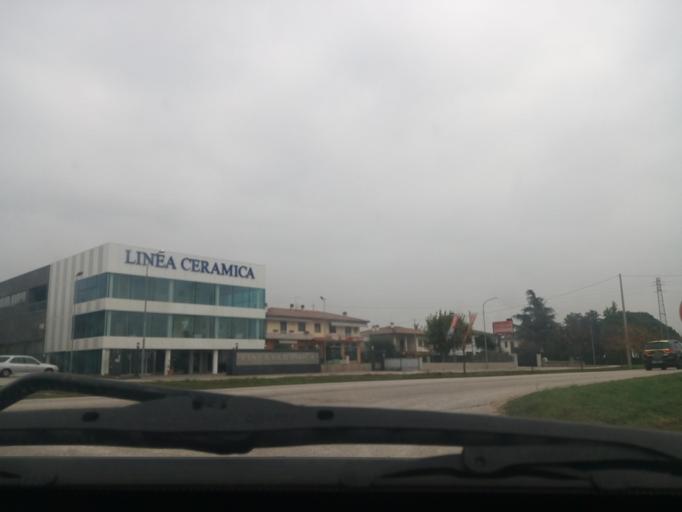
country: IT
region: Veneto
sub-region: Provincia di Vicenza
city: Sarcedo
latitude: 45.6924
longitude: 11.5275
